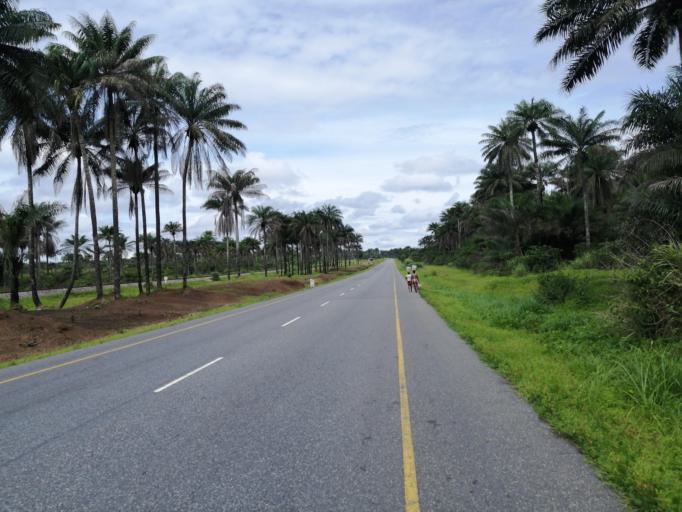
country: SL
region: Northern Province
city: Port Loko
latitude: 8.7268
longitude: -12.9528
